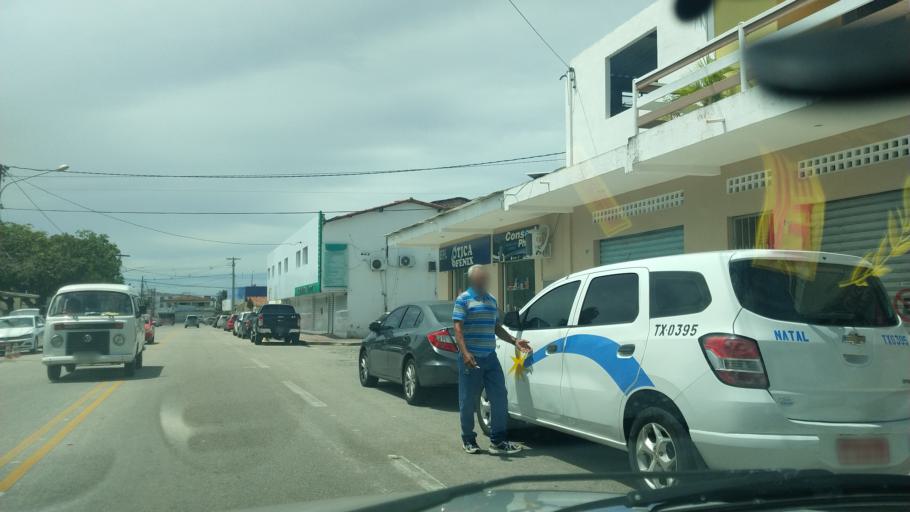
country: BR
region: Rio Grande do Norte
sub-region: Natal
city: Natal
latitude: -5.8257
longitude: -35.2363
